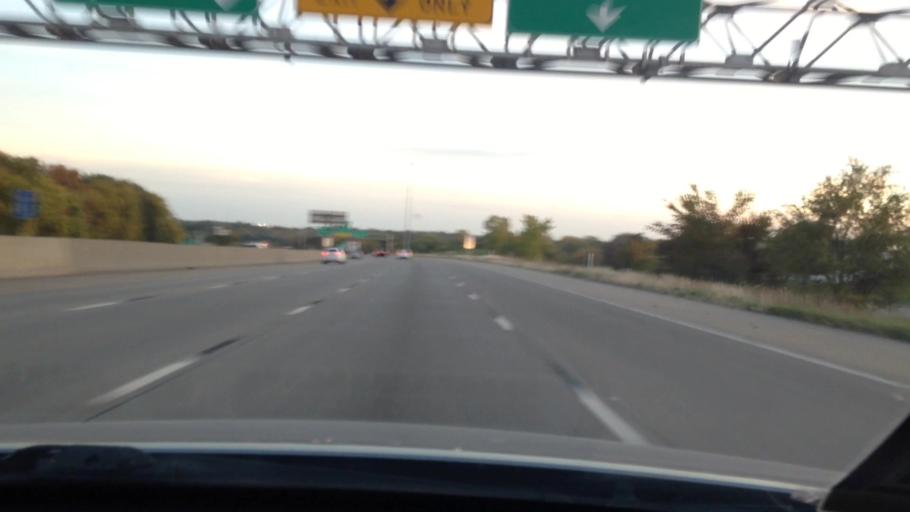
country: US
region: Kansas
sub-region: Johnson County
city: Merriam
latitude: 39.0501
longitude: -94.6792
